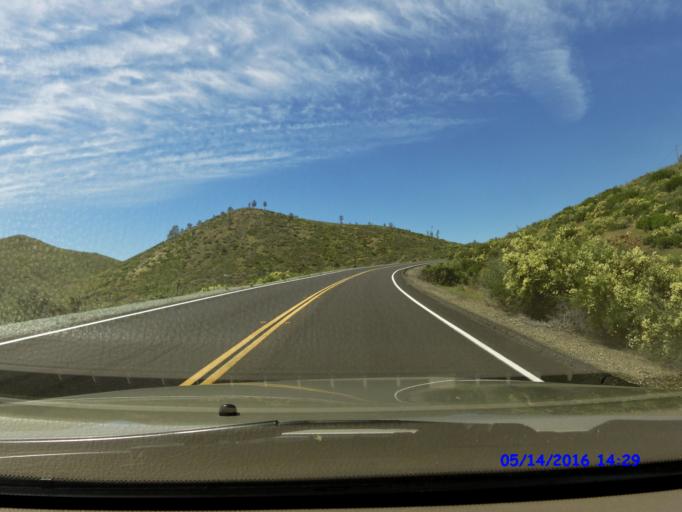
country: US
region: California
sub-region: Tuolumne County
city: Tuolumne City
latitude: 37.7435
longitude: -120.2425
